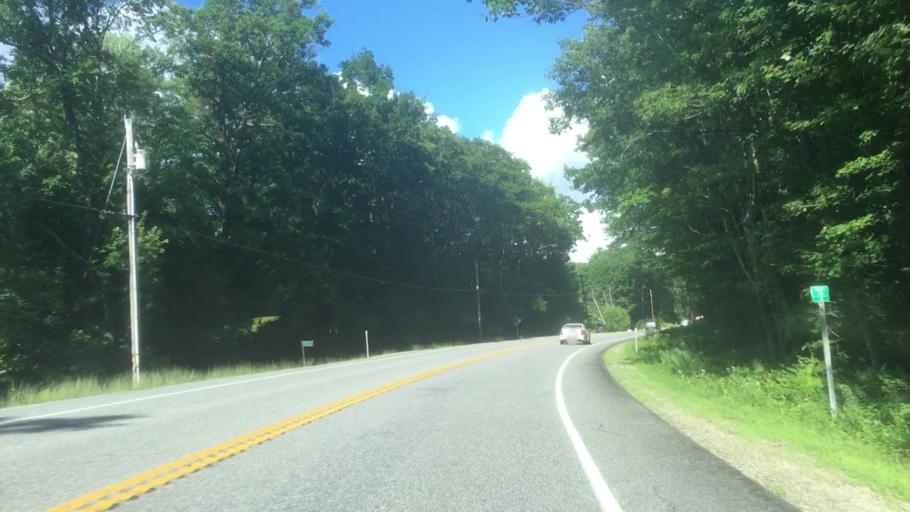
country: US
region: New Hampshire
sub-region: Hillsborough County
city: Antrim
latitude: 43.0752
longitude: -72.0142
